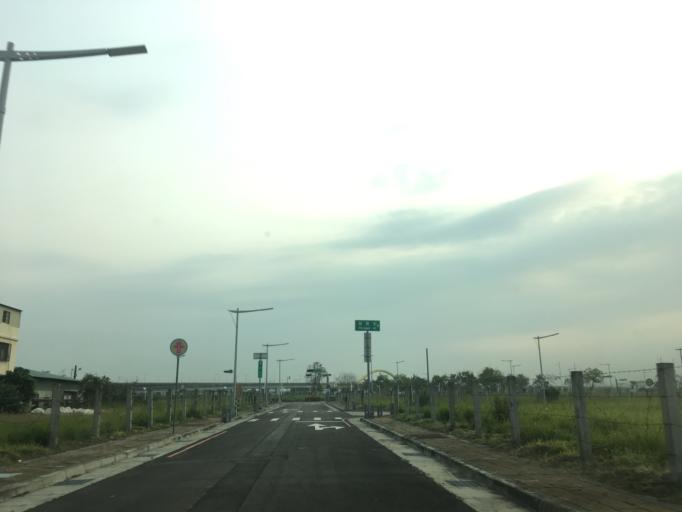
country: TW
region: Taiwan
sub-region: Taichung City
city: Taichung
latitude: 24.1972
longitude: 120.6664
